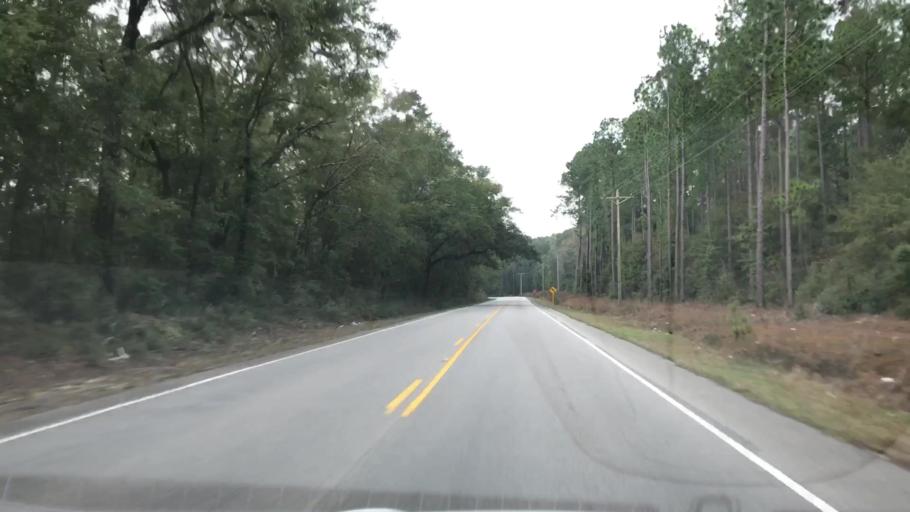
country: US
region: South Carolina
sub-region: Jasper County
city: Ridgeland
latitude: 32.4921
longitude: -80.8865
